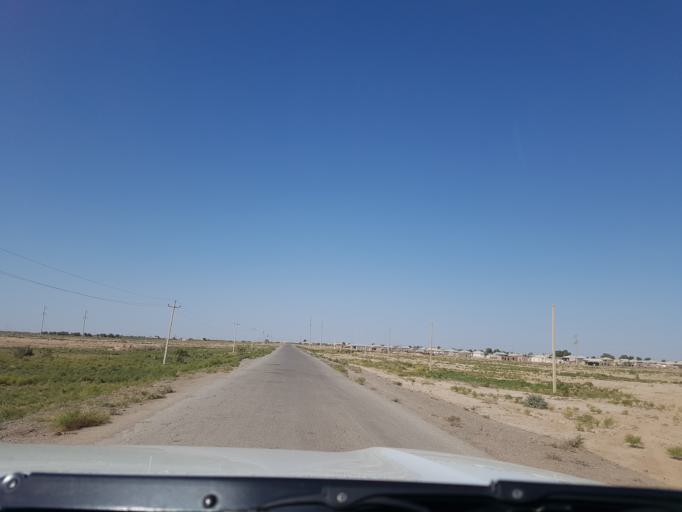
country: IR
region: Razavi Khorasan
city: Sarakhs
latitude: 36.5060
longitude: 61.2534
